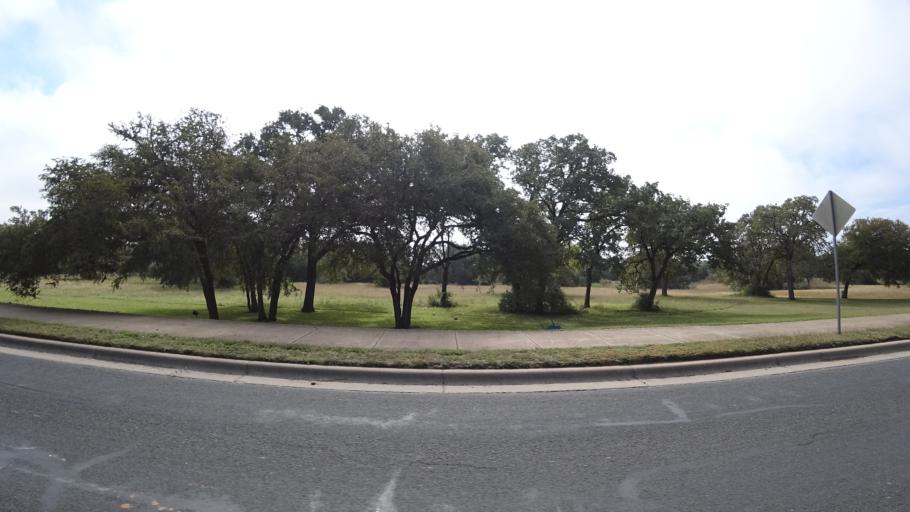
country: US
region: Texas
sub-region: Travis County
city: Shady Hollow
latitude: 30.2003
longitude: -97.8740
